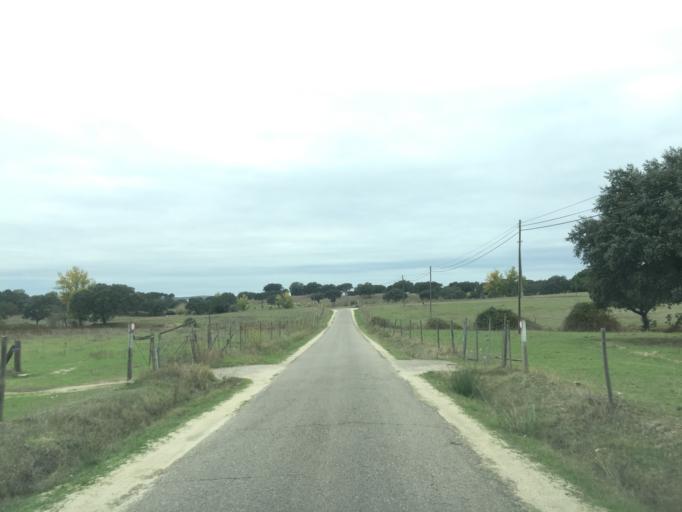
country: PT
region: Portalegre
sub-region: Fronteira
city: Vale da Amoreira
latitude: 39.0509
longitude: -7.7781
